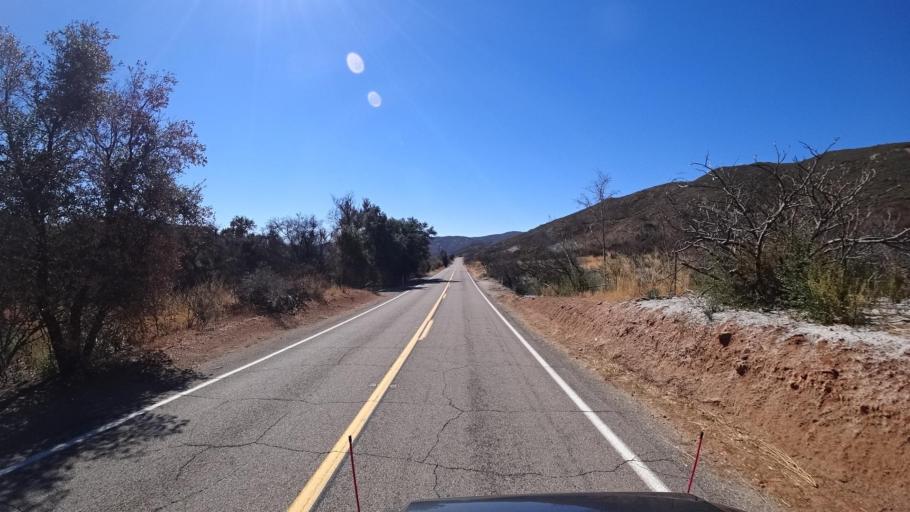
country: US
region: California
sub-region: San Diego County
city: Alpine
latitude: 32.7189
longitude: -116.7051
